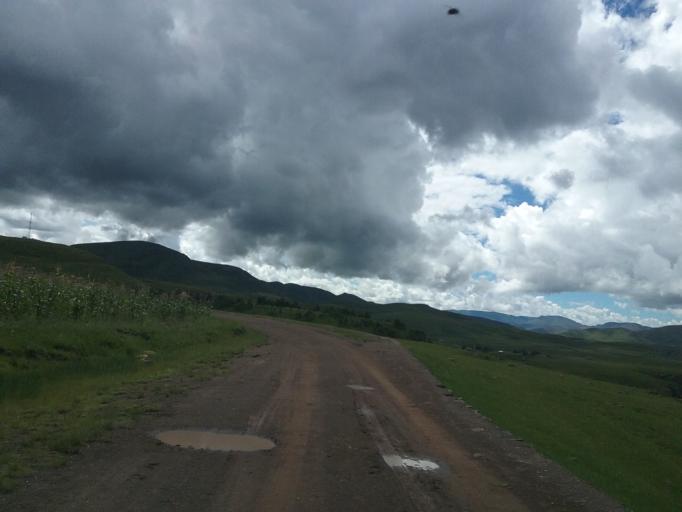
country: LS
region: Maseru
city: Nako
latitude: -29.8776
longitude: 28.0472
